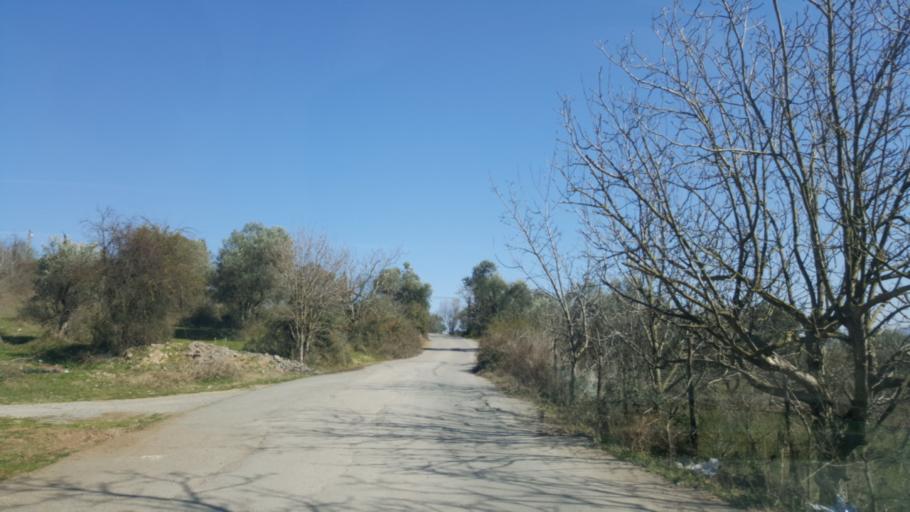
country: TR
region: Kocaeli
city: Tavsancil
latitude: 40.7770
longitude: 29.5739
